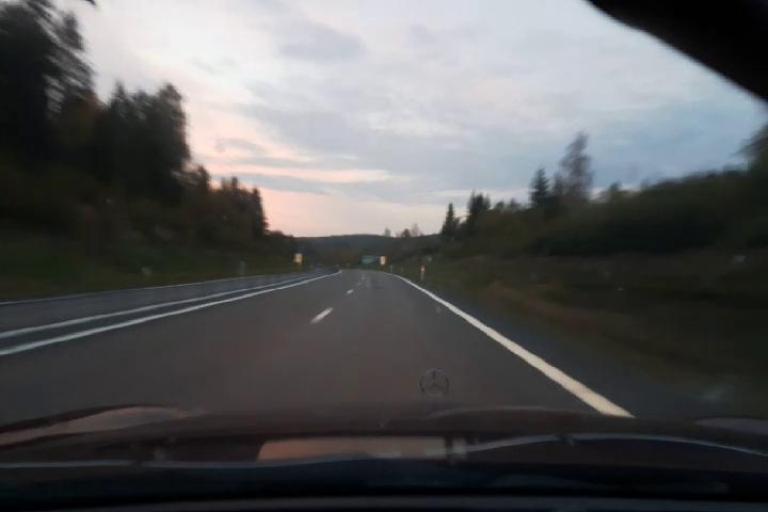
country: SE
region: Vaesternorrland
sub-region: Kramfors Kommun
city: Nordingra
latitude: 62.9240
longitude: 18.0992
